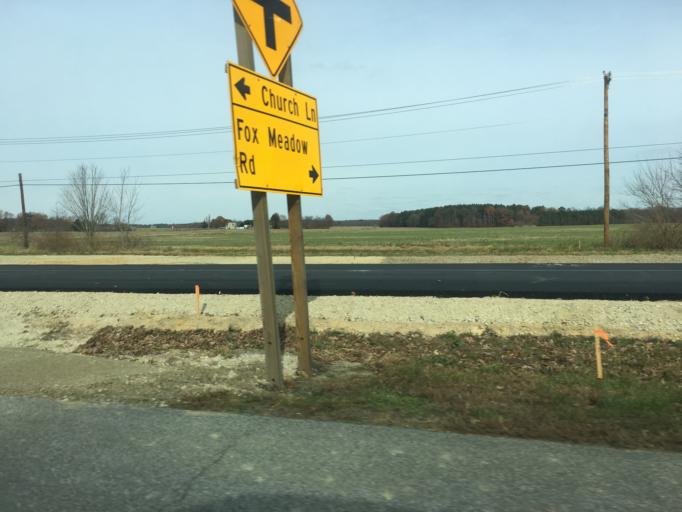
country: US
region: Maryland
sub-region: Queen Anne's County
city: Centreville
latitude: 38.9297
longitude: -76.0101
